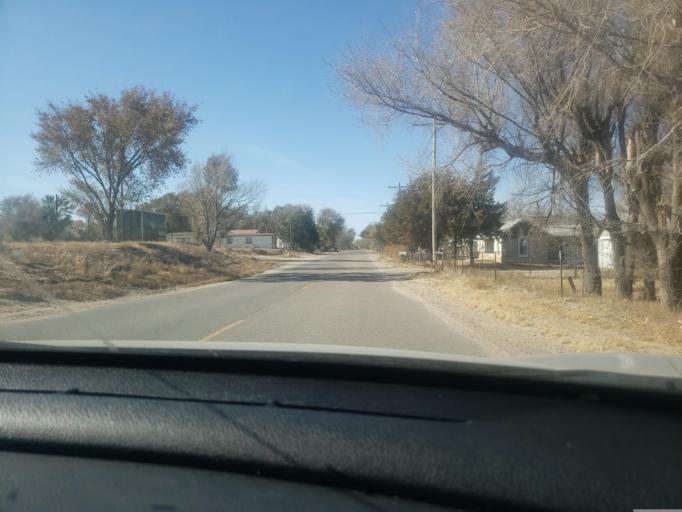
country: US
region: Kansas
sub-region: Finney County
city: Garden City
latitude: 37.9512
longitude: -100.8669
